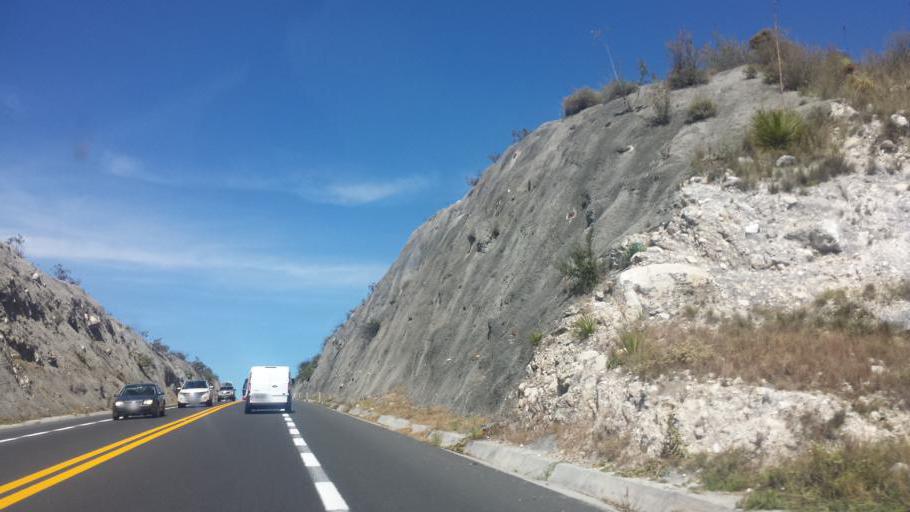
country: MX
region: Puebla
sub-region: San Jose Miahuatlan
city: San Pedro Tetitlan
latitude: 17.9973
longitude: -97.3548
